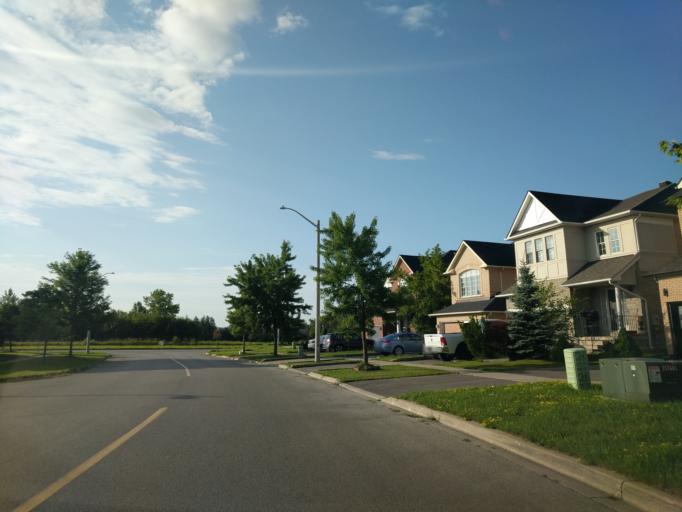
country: CA
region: Ontario
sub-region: York
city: Richmond Hill
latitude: 43.8944
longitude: -79.4459
